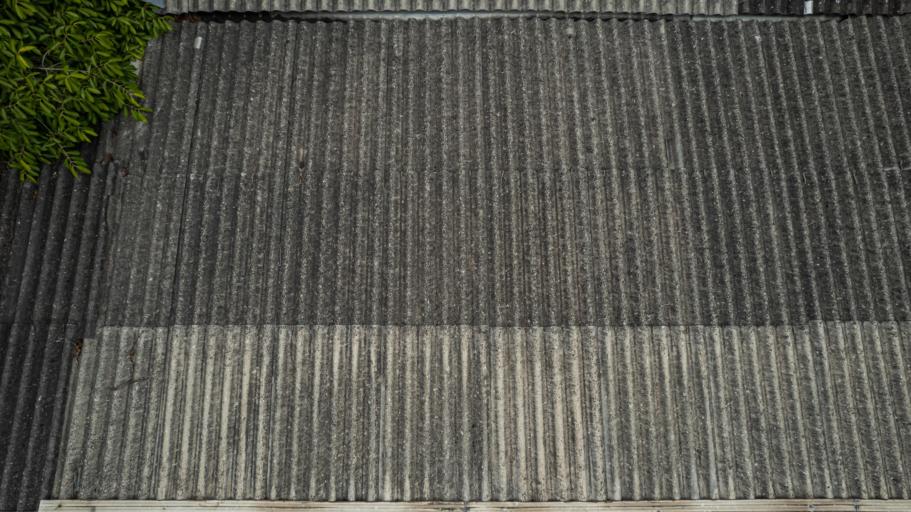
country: BR
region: Sao Paulo
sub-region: Pindamonhangaba
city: Pindamonhangaba
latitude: -22.9045
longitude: -45.3510
